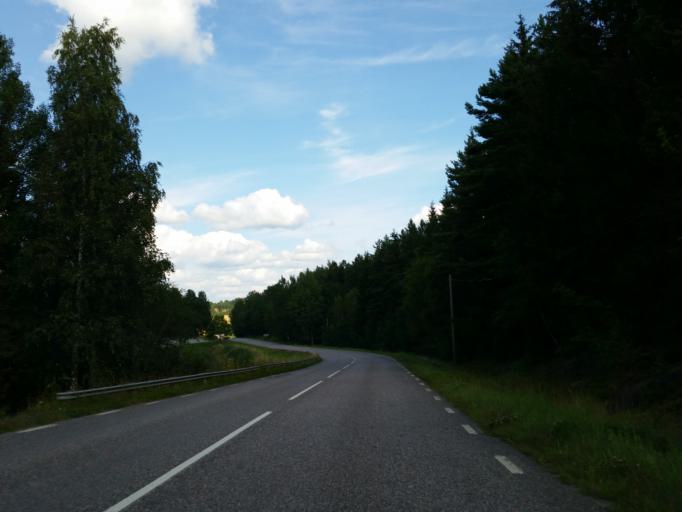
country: SE
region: Stockholm
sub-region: Sodertalje Kommun
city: Pershagen
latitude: 59.0118
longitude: 17.6630
